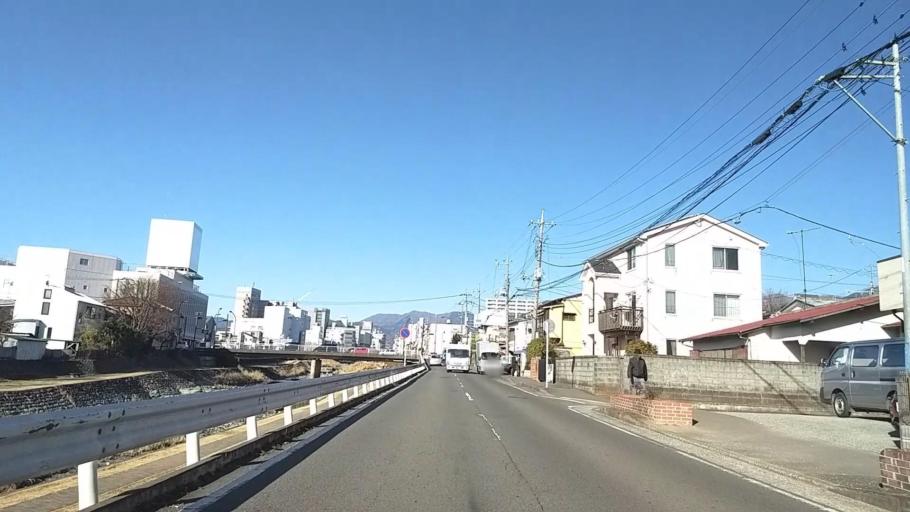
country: JP
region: Kanagawa
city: Hadano
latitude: 35.3688
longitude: 139.2327
